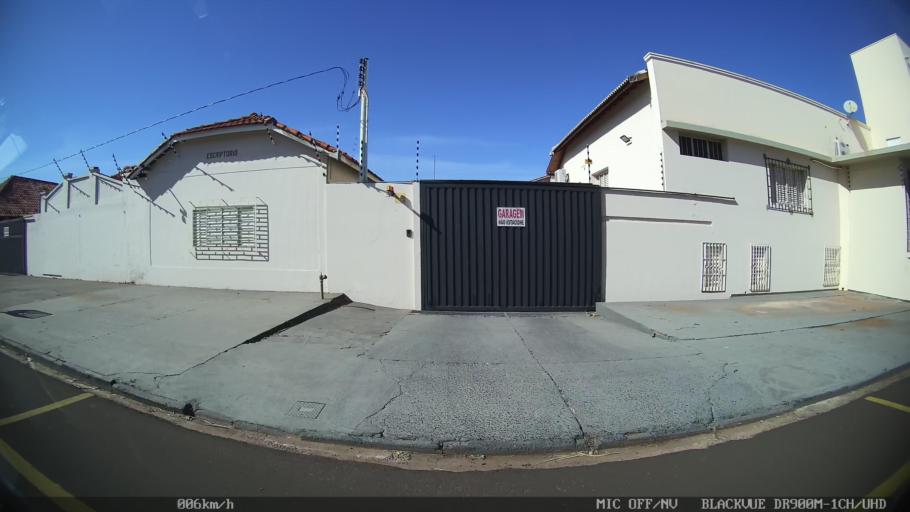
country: BR
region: Sao Paulo
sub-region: Olimpia
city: Olimpia
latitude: -20.7354
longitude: -48.9172
